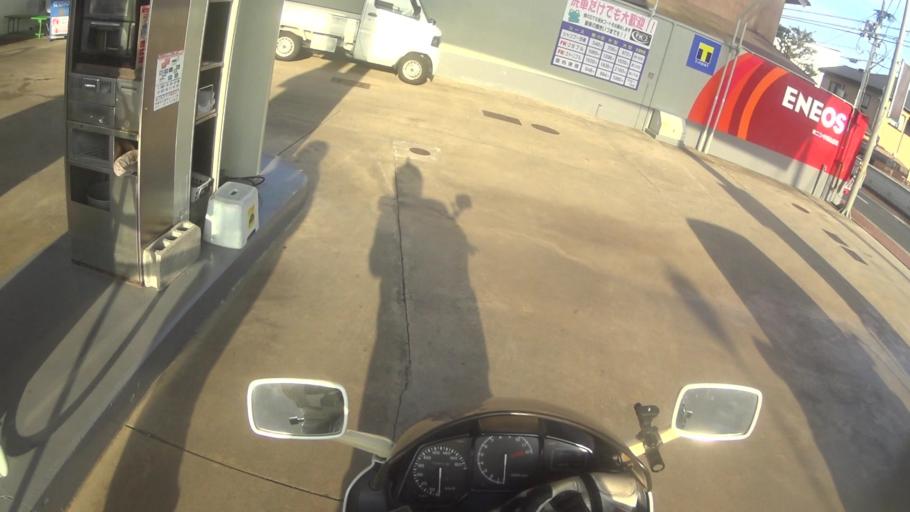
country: JP
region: Kyoto
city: Miyazu
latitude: 35.6276
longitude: 135.0686
